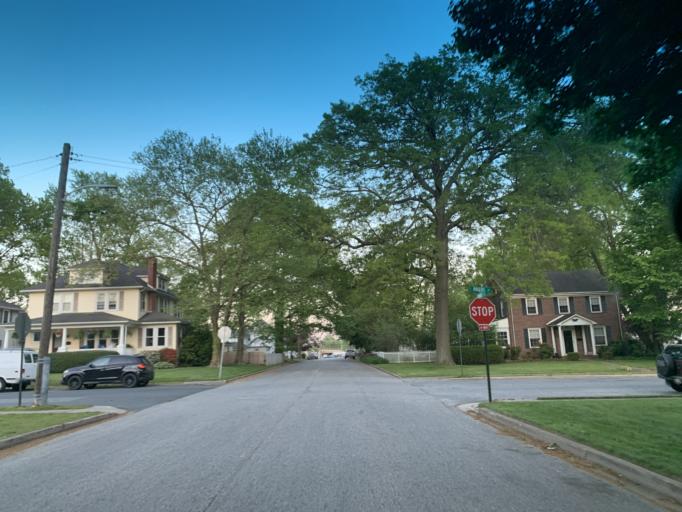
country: US
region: Maryland
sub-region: Harford County
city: Aberdeen
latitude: 39.5079
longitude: -76.1687
